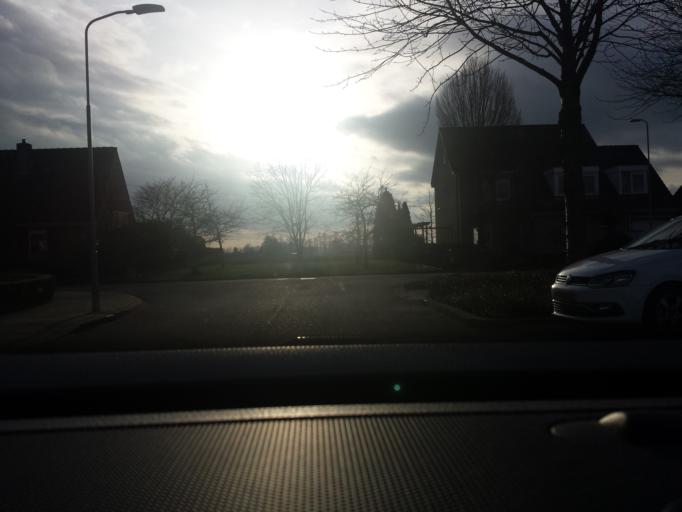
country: NL
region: Gelderland
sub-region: Gemeente Duiven
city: Duiven
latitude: 51.9355
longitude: 6.0134
